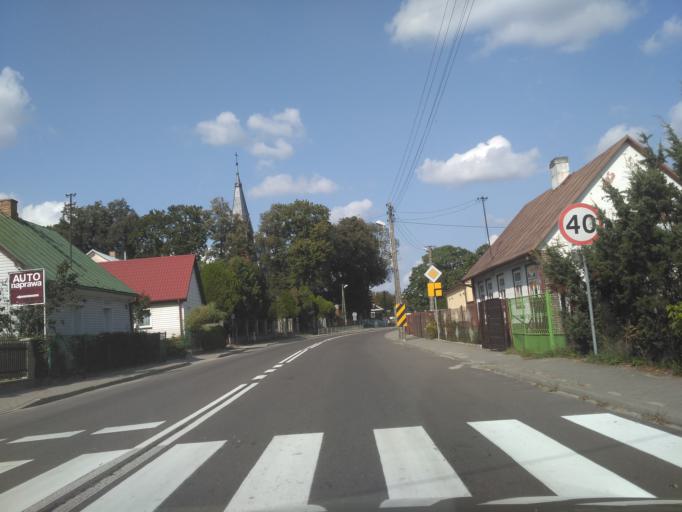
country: PL
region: Lublin Voivodeship
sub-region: Powiat chelmski
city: Rejowiec
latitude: 51.0964
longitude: 23.2846
